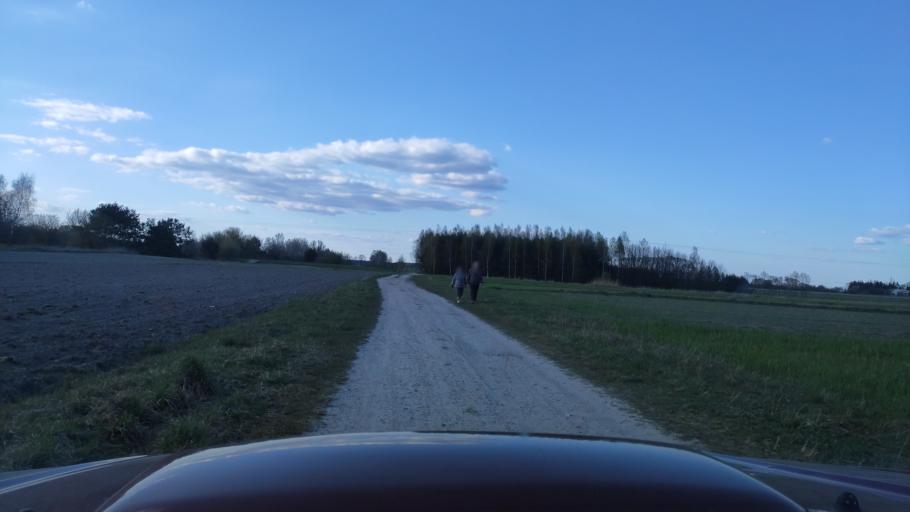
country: PL
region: Masovian Voivodeship
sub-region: Powiat zwolenski
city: Zwolen
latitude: 51.3666
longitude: 21.5753
